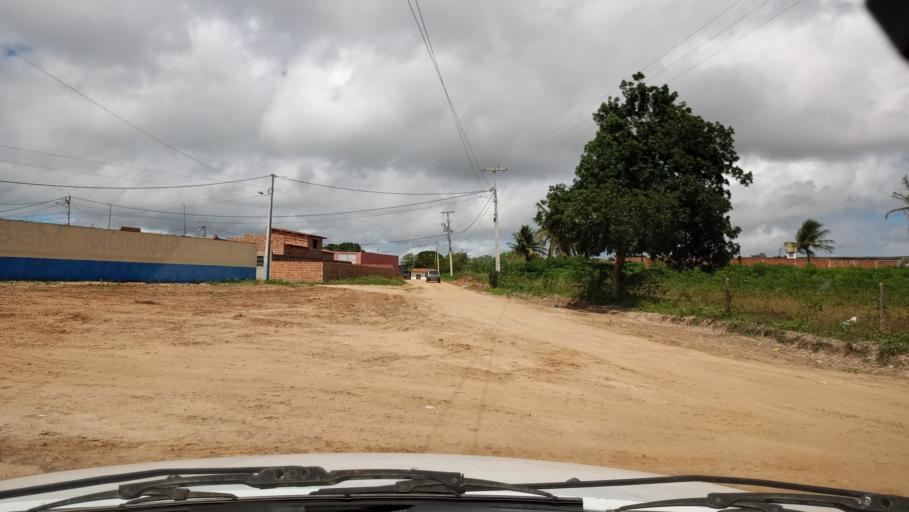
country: BR
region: Rio Grande do Norte
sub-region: Brejinho
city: Brejinho
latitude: -6.1570
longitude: -35.4416
